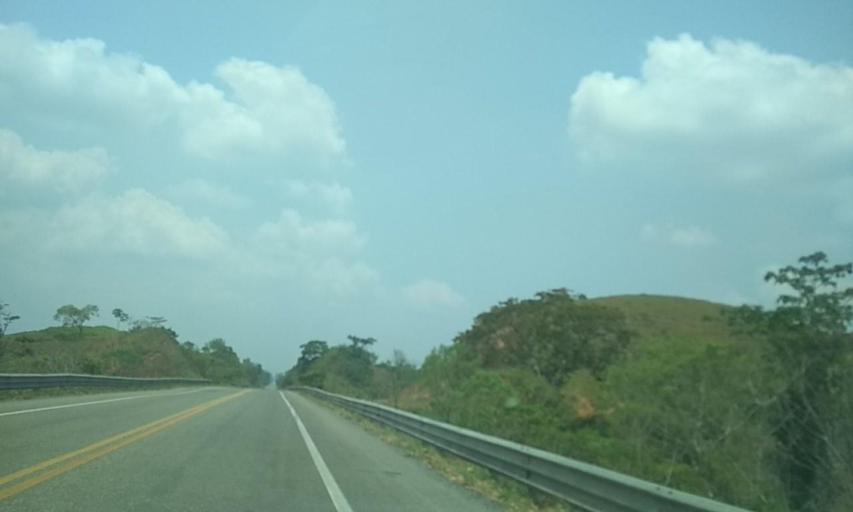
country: MX
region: Tabasco
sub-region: Huimanguillo
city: Francisco Rueda
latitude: 17.6580
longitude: -93.8492
